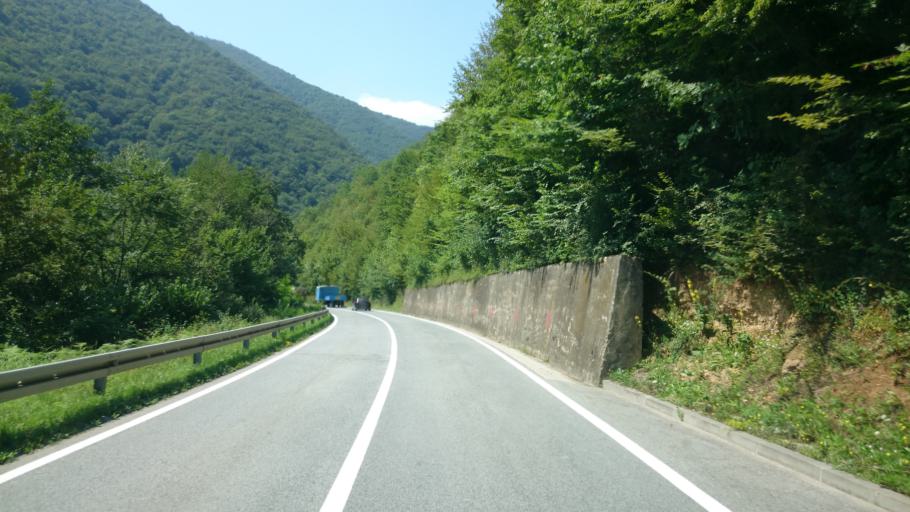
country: BA
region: Federation of Bosnia and Herzegovina
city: Donji Vakuf
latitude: 44.2109
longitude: 17.3215
